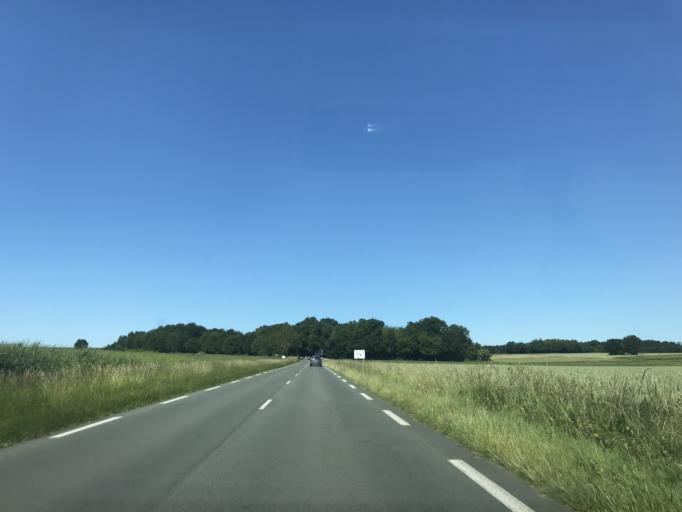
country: FR
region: Poitou-Charentes
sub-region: Departement de la Charente-Maritime
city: Cozes
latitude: 45.5793
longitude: -0.7961
